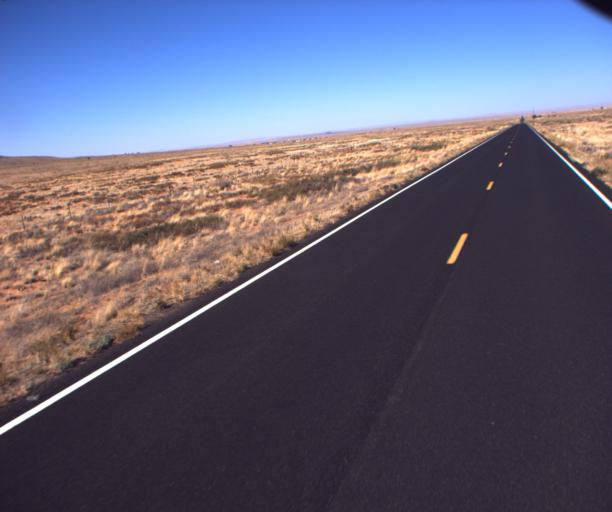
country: US
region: Arizona
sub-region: Navajo County
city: Dilkon
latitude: 35.4780
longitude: -110.4263
